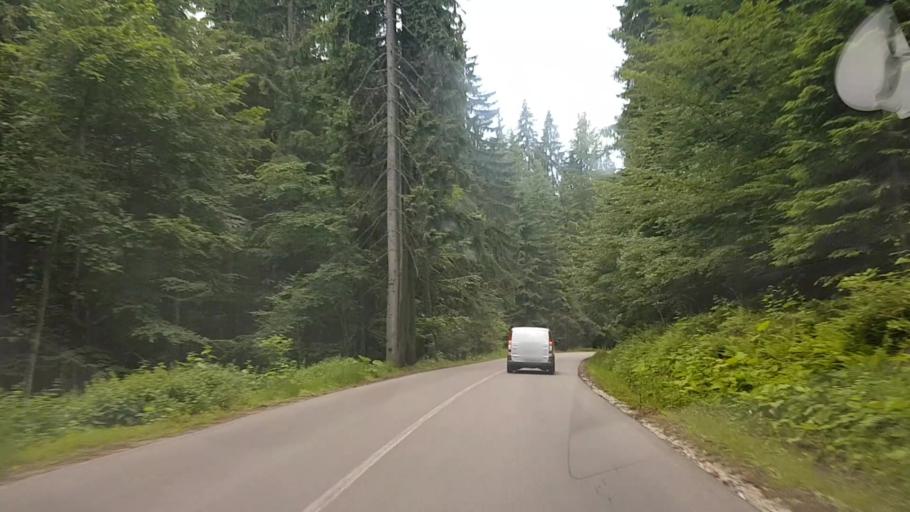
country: RO
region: Harghita
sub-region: Comuna Varsag
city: Varsag
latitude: 46.6694
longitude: 25.3255
